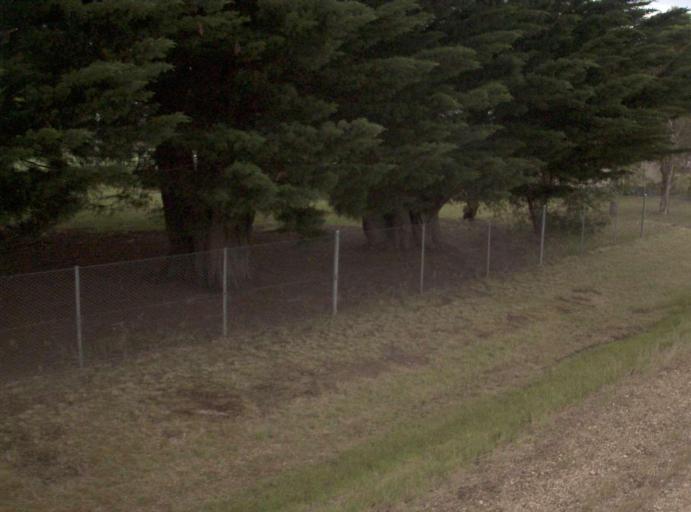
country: AU
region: Victoria
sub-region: East Gippsland
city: Bairnsdale
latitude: -38.0017
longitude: 147.3883
